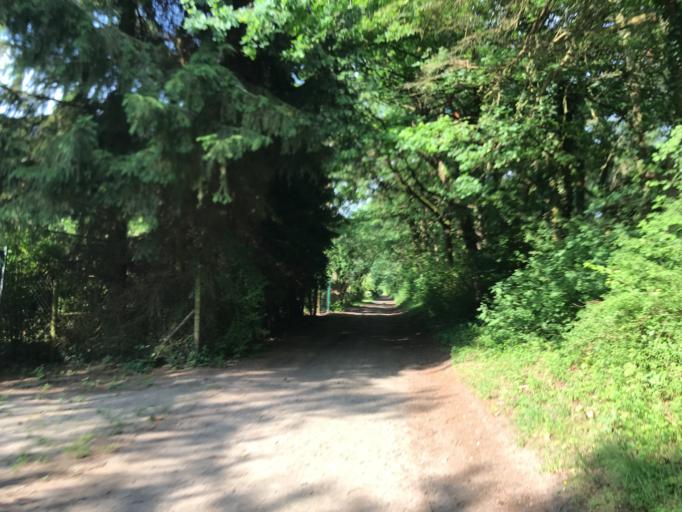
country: DE
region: Hesse
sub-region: Regierungsbezirk Darmstadt
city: Eltville
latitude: 50.0117
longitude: 8.1363
